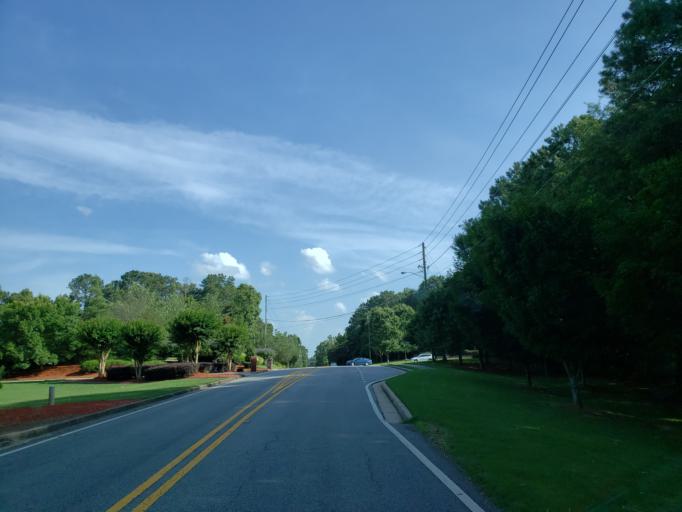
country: US
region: Georgia
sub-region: Cobb County
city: Powder Springs
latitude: 33.9245
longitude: -84.7059
